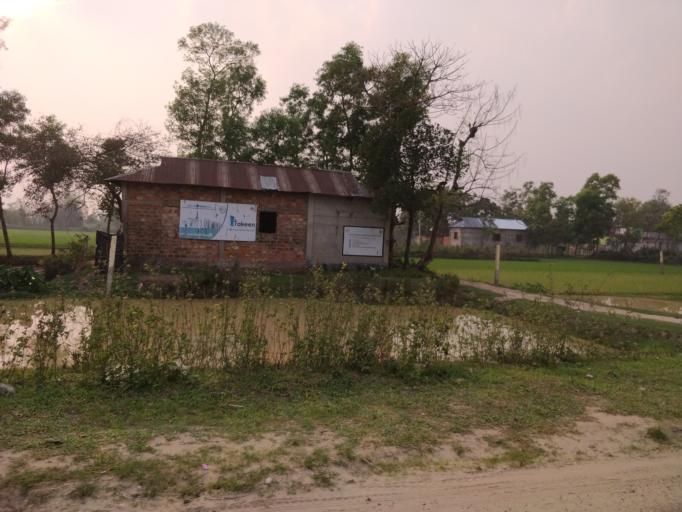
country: BD
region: Sylhet
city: Habiganj
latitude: 24.1446
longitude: 91.3512
